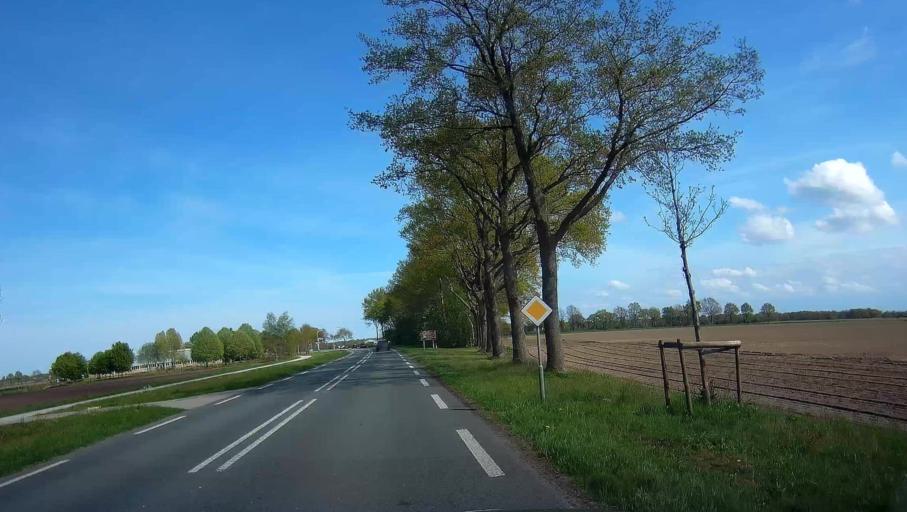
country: NL
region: Drenthe
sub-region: Gemeente Borger-Odoorn
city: Borger
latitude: 52.9101
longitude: 6.7417
